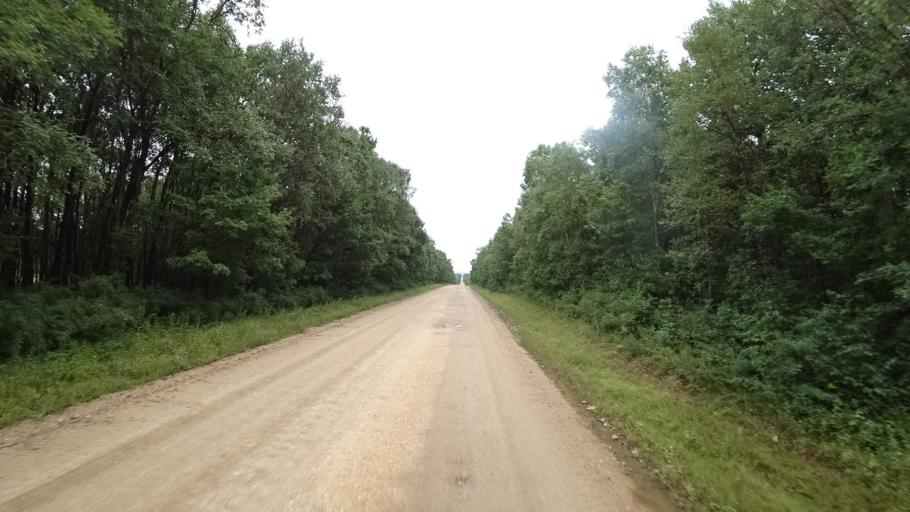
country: RU
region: Primorskiy
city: Ivanovka
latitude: 44.0329
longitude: 132.5317
